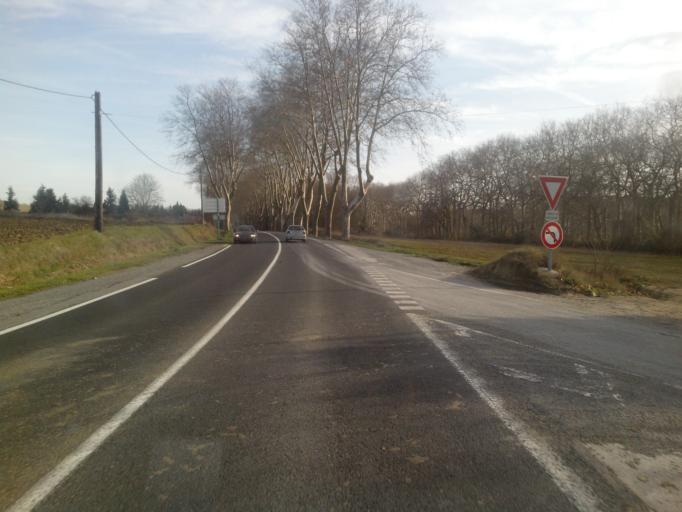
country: FR
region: Languedoc-Roussillon
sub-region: Departement de l'Aude
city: Castelnaudary
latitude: 43.3041
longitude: 1.9817
